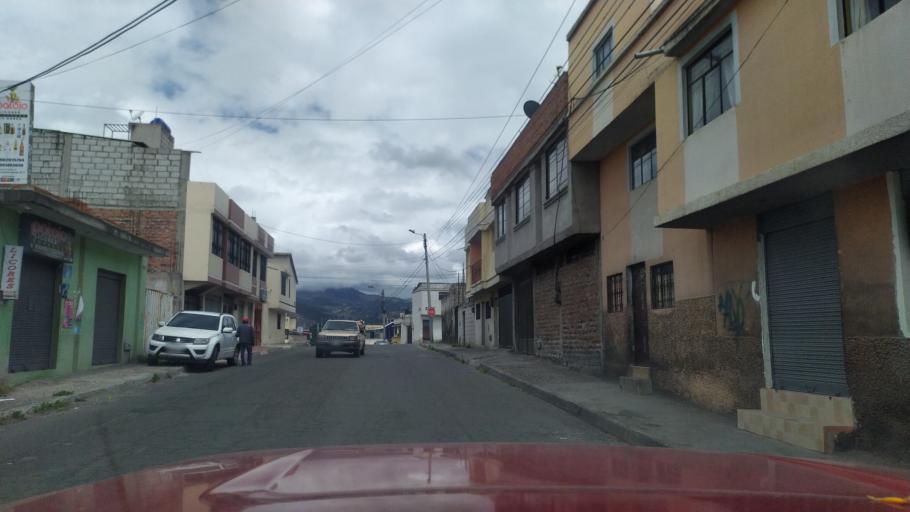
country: EC
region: Chimborazo
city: Riobamba
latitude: -1.6650
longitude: -78.6398
